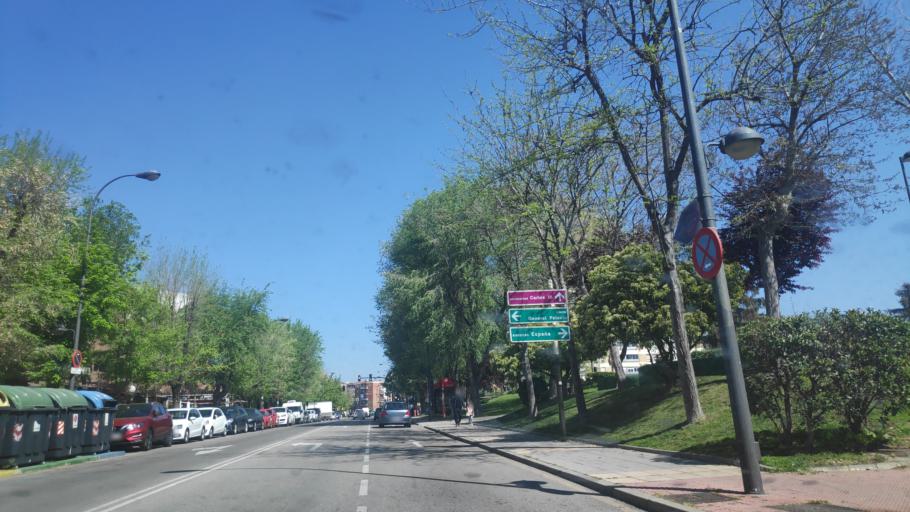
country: ES
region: Madrid
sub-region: Provincia de Madrid
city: Getafe
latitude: 40.3078
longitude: -3.7250
